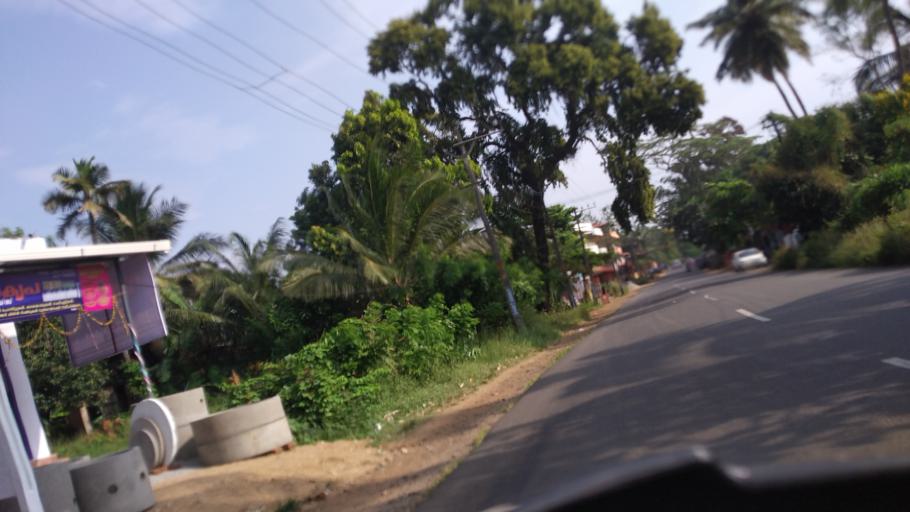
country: IN
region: Kerala
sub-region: Thrissur District
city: Chelakara
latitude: 10.5964
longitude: 76.5016
